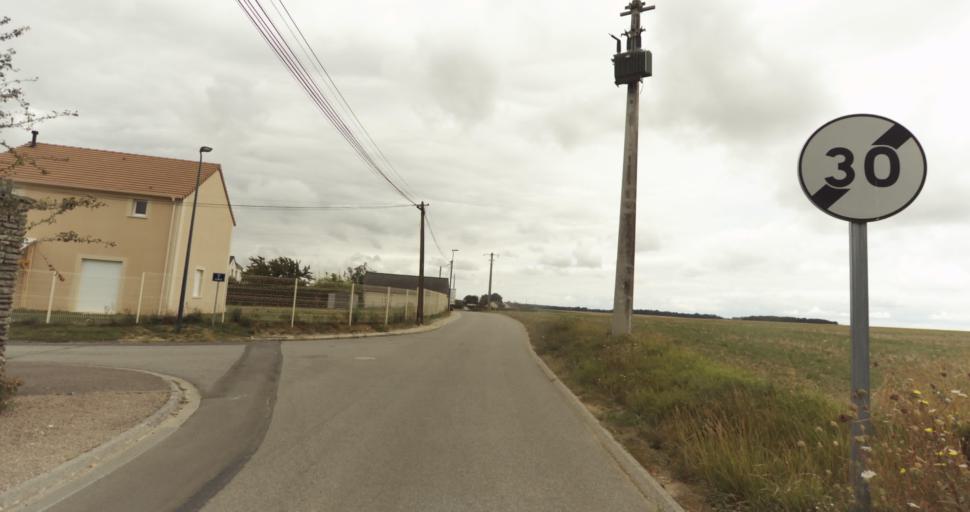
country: FR
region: Haute-Normandie
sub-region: Departement de l'Eure
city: Menilles
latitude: 49.0241
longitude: 1.3063
